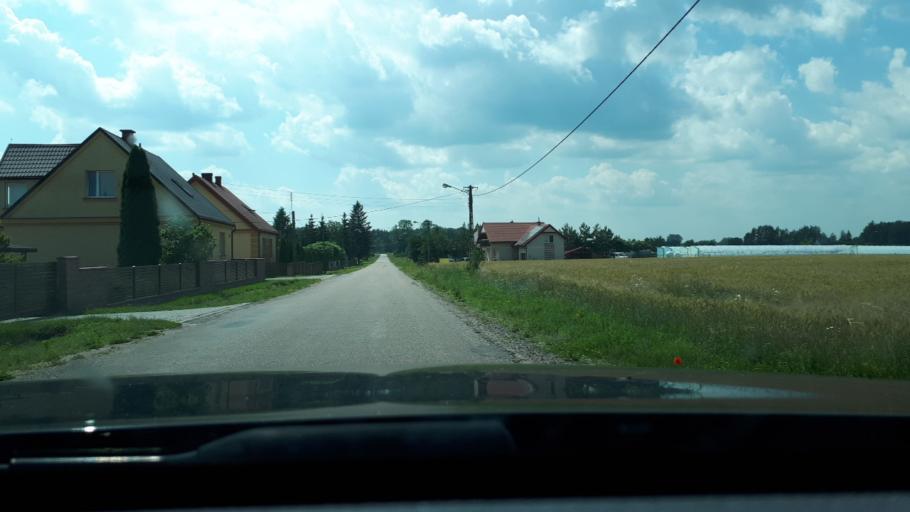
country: PL
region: Podlasie
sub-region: Powiat bialostocki
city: Lapy
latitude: 53.1068
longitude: 22.8734
